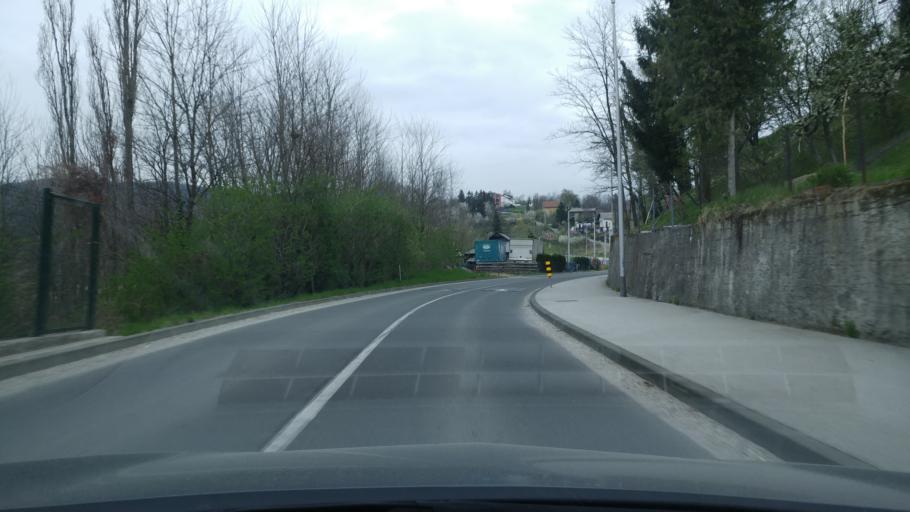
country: HR
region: Grad Zagreb
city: Stenjevec
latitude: 45.8224
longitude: 15.8731
